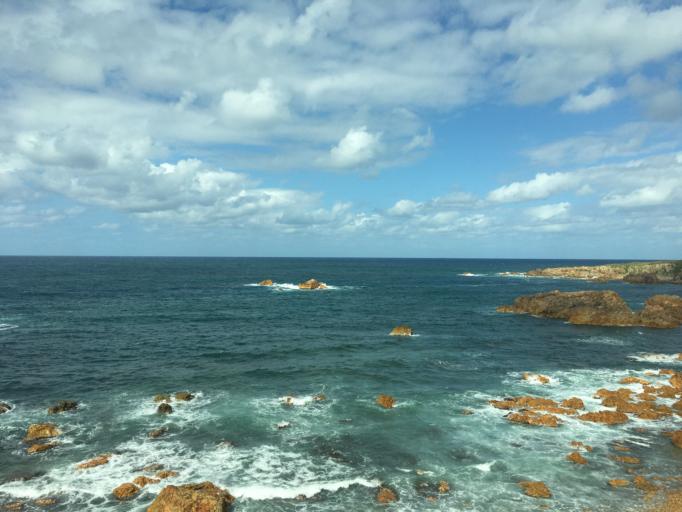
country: JP
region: Aomori
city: Shimokizukuri
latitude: 40.6642
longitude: 139.9388
